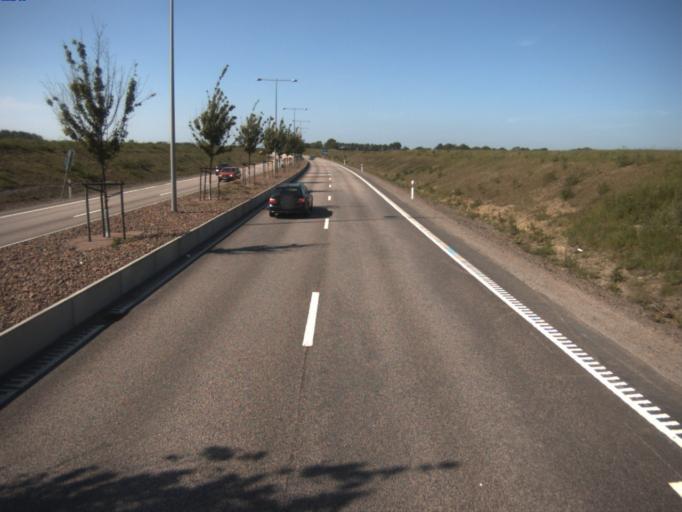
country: SE
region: Skane
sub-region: Helsingborg
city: Gantofta
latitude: 56.0324
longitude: 12.7615
